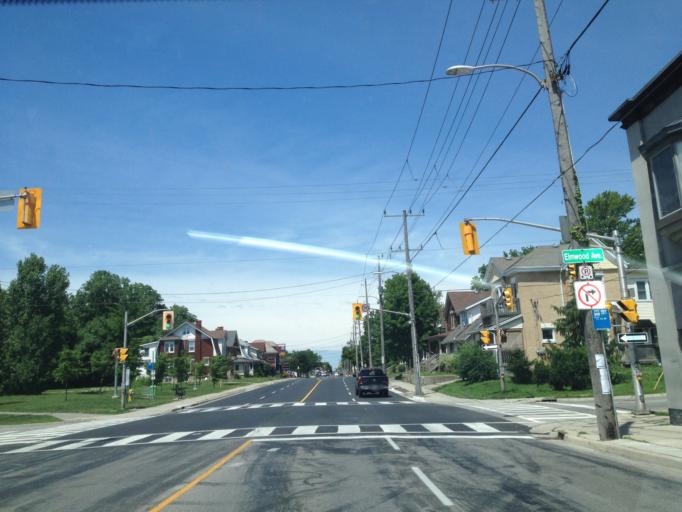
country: CA
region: Ontario
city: London
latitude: 42.9696
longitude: -81.2618
